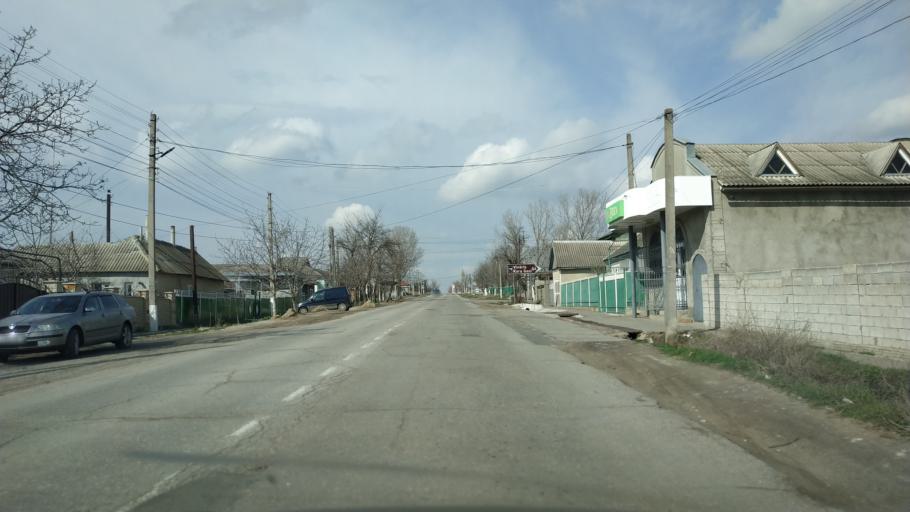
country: MD
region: Gagauzia
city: Vulcanesti
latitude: 45.6940
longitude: 28.4047
